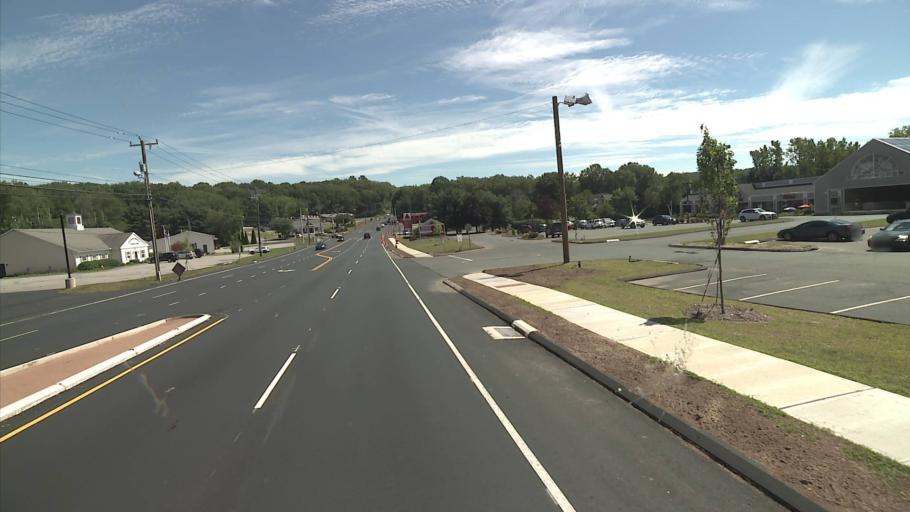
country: US
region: Connecticut
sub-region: Tolland County
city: Tolland
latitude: 41.8605
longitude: -72.3547
